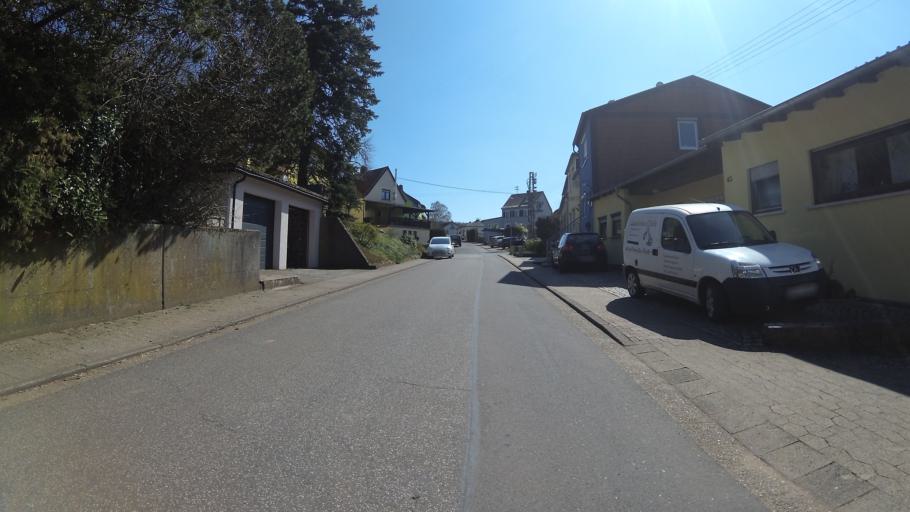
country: DE
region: Rheinland-Pfalz
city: Breitenbach
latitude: 49.4188
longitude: 7.2424
